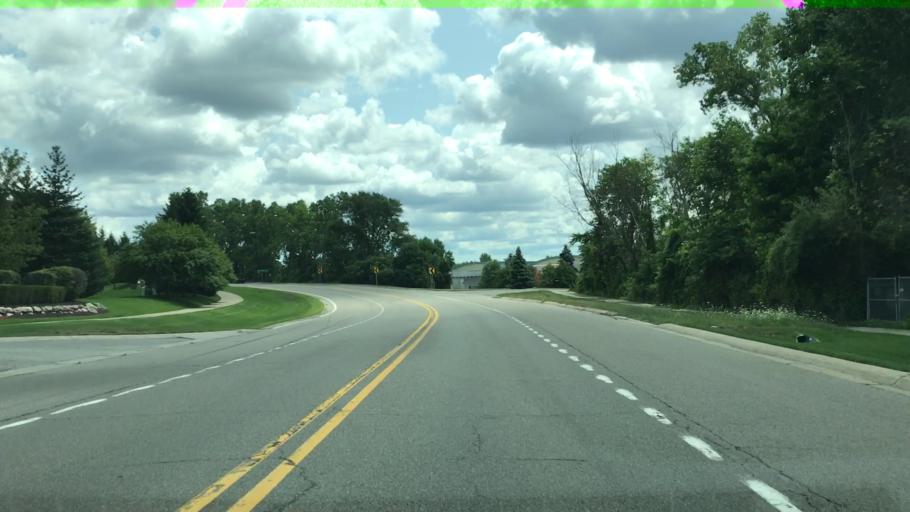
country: US
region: Michigan
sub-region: Oakland County
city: Rochester
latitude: 42.6835
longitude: -83.0975
